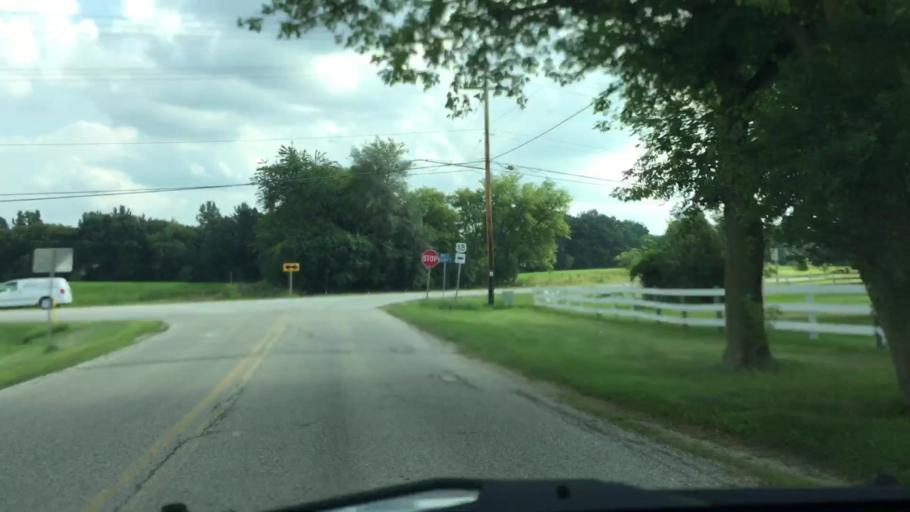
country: US
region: Wisconsin
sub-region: Waukesha County
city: Wales
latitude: 43.0194
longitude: -88.3642
